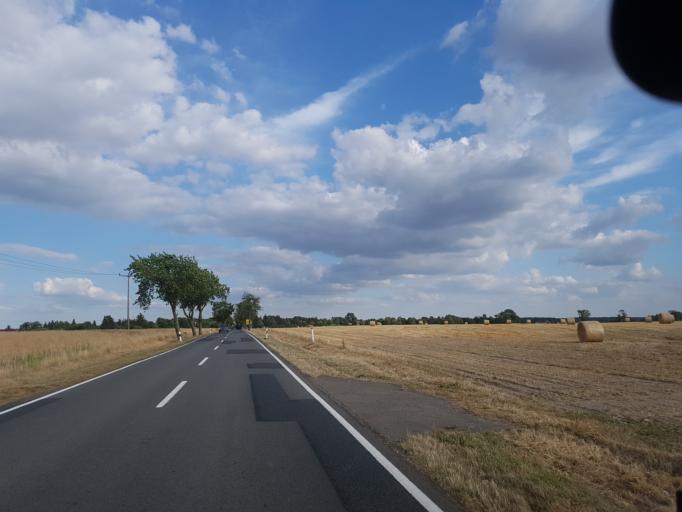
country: DE
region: Brandenburg
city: Schlieben
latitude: 51.7304
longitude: 13.3093
